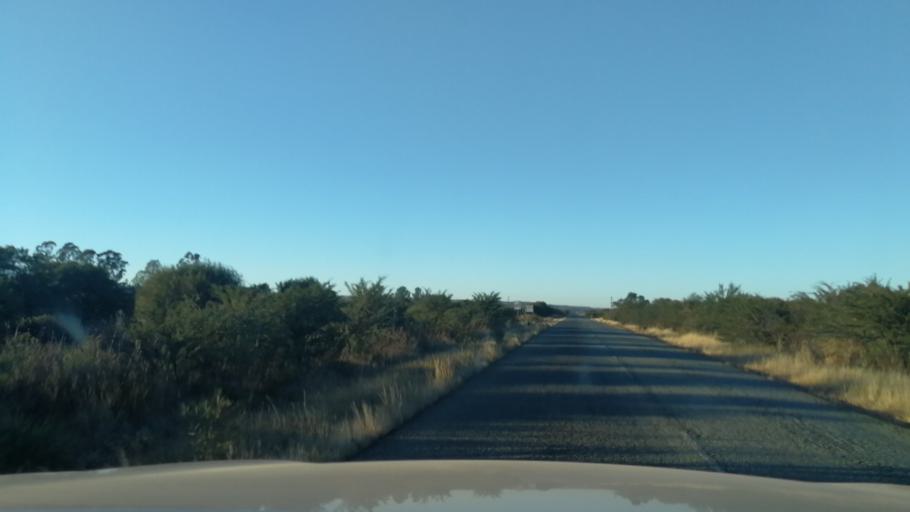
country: ZA
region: North-West
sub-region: Bojanala Platinum District Municipality
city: Koster
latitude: -25.7019
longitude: 26.7360
